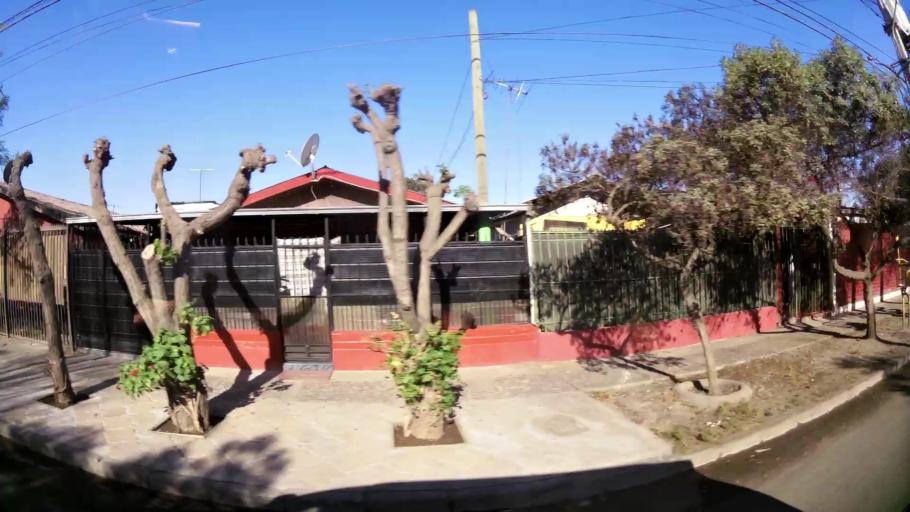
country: CL
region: Santiago Metropolitan
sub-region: Provincia de Talagante
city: Penaflor
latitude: -33.6060
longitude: -70.8683
